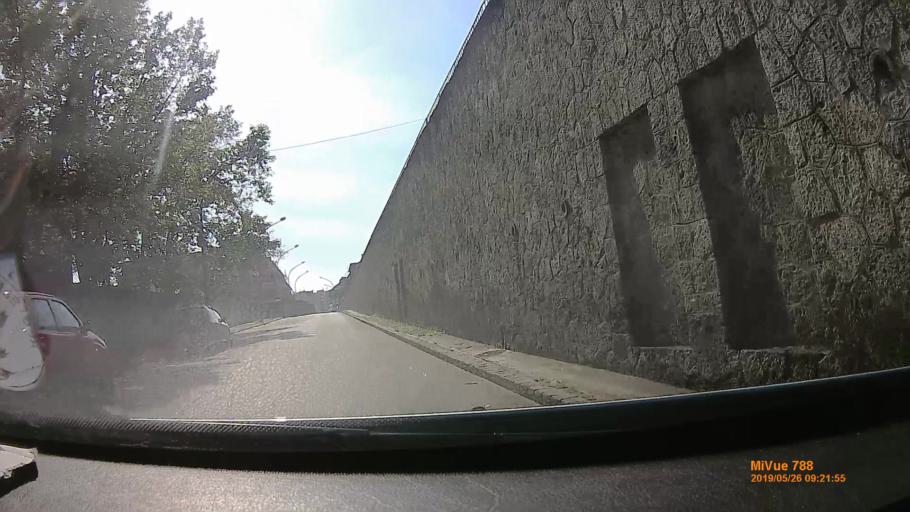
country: HU
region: Borsod-Abauj-Zemplen
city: Miskolc
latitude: 48.1010
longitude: 20.7803
